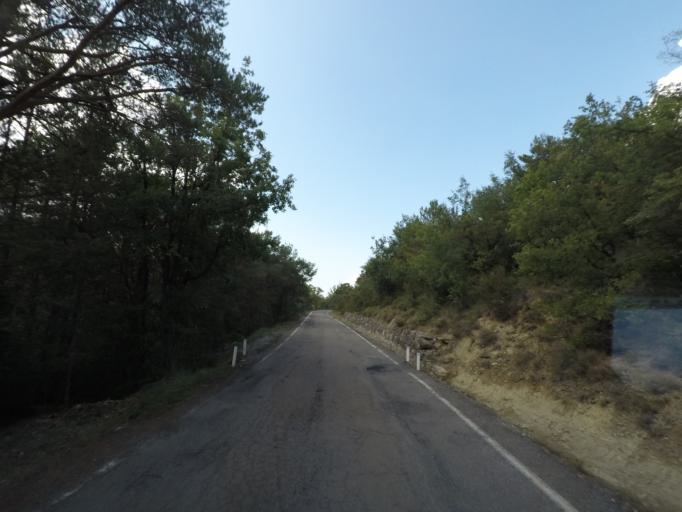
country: ES
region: Aragon
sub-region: Provincia de Huesca
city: Yebra de Basa
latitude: 42.3957
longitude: -0.3263
